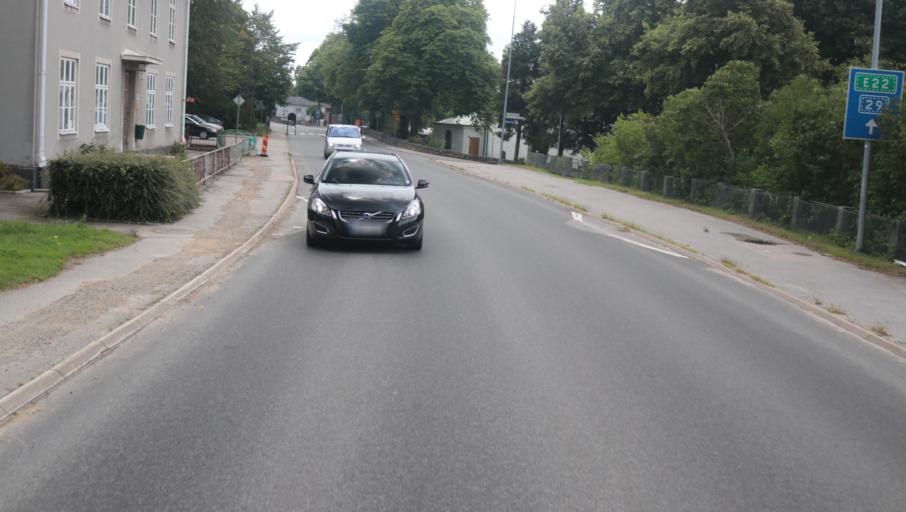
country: SE
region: Blekinge
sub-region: Karlshamns Kommun
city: Karlshamn
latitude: 56.2068
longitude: 14.8338
